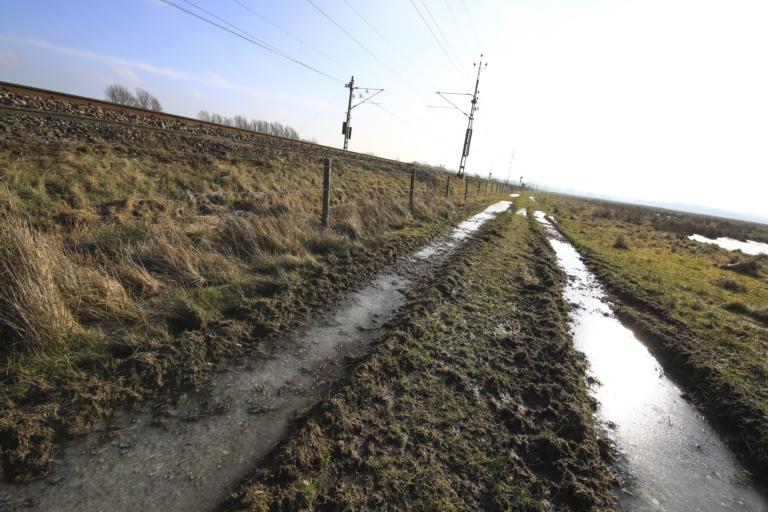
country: SE
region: Halland
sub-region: Kungsbacka Kommun
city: Frillesas
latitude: 57.2232
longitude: 12.2160
